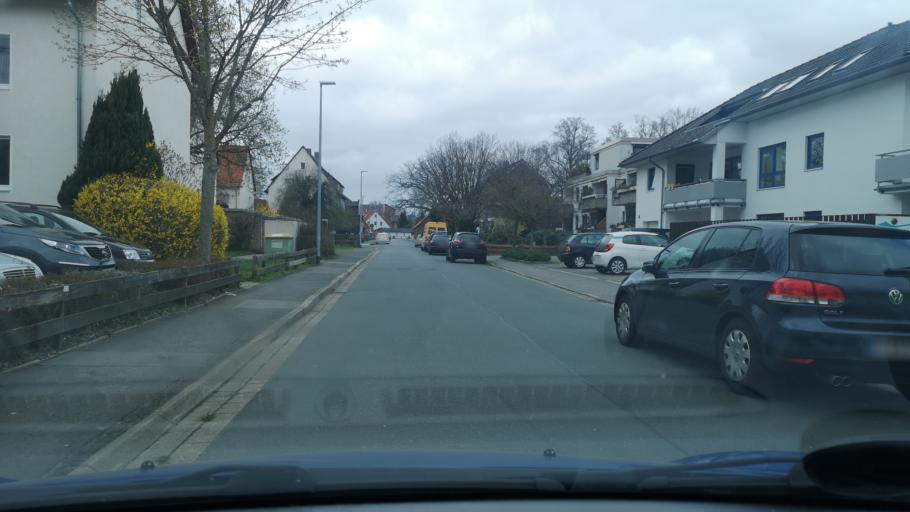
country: DE
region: Lower Saxony
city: Langenhagen
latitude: 52.4353
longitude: 9.7094
